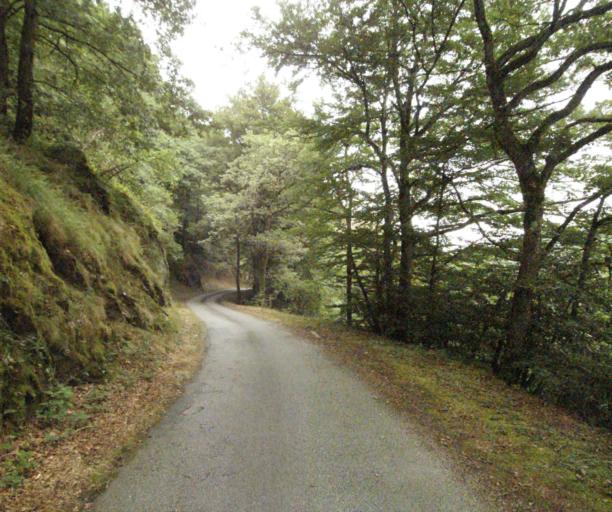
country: FR
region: Midi-Pyrenees
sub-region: Departement du Tarn
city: Soreze
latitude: 43.4195
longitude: 2.0851
